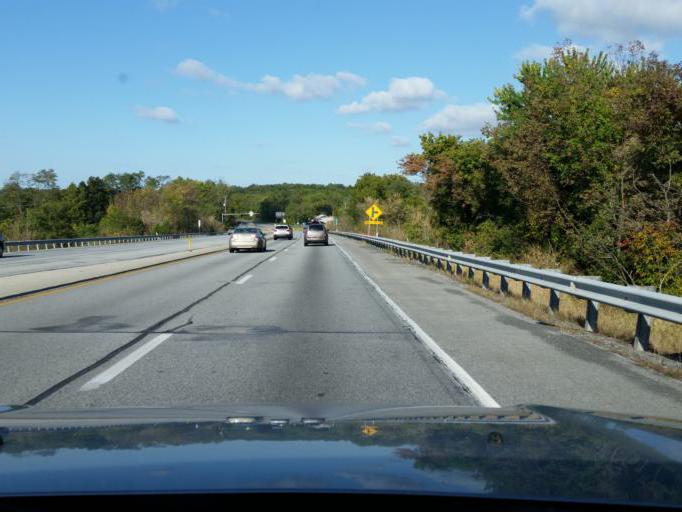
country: US
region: Pennsylvania
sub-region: York County
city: Dillsburg
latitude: 40.1341
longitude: -77.0164
